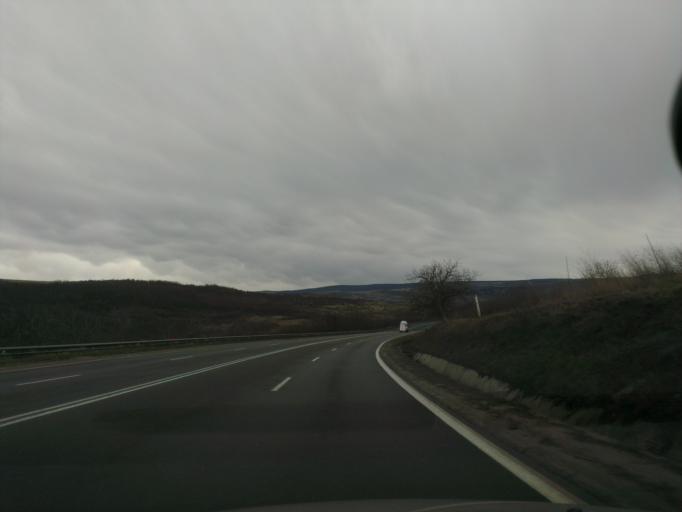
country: MD
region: Laloveni
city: Ialoveni
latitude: 46.9378
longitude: 28.7038
